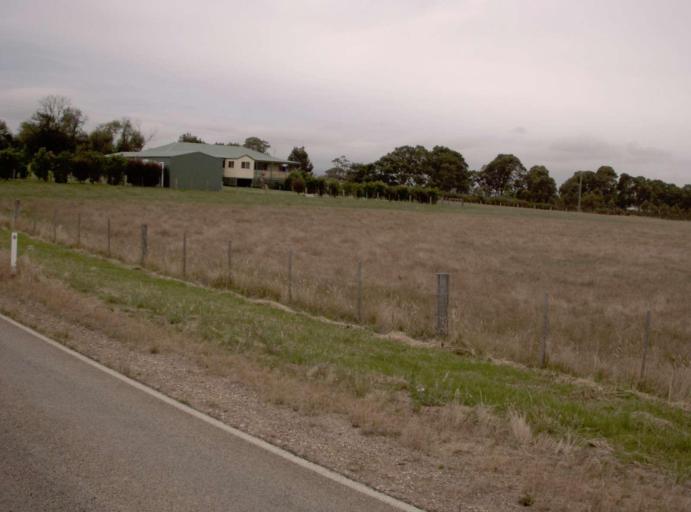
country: AU
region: Victoria
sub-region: East Gippsland
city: Bairnsdale
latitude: -37.8179
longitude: 147.4361
